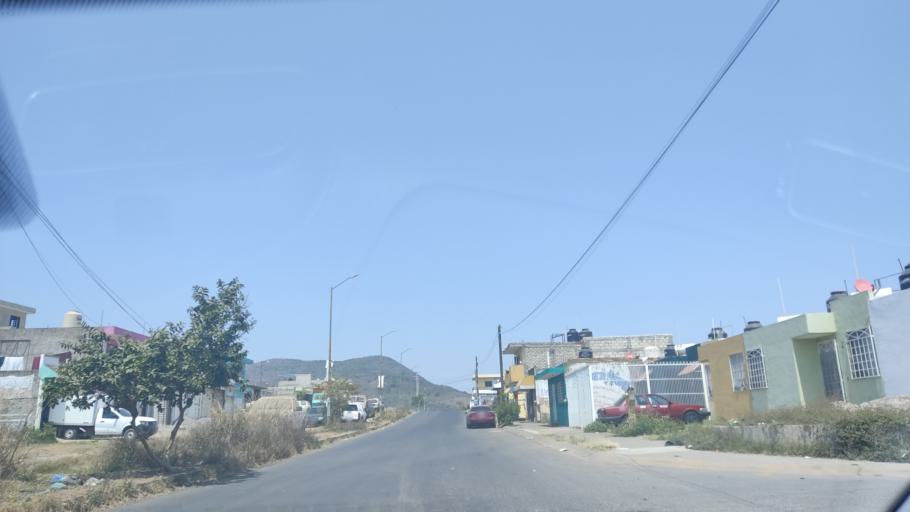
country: MX
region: Nayarit
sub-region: Tepic
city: La Corregidora
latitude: 21.4904
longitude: -104.8172
